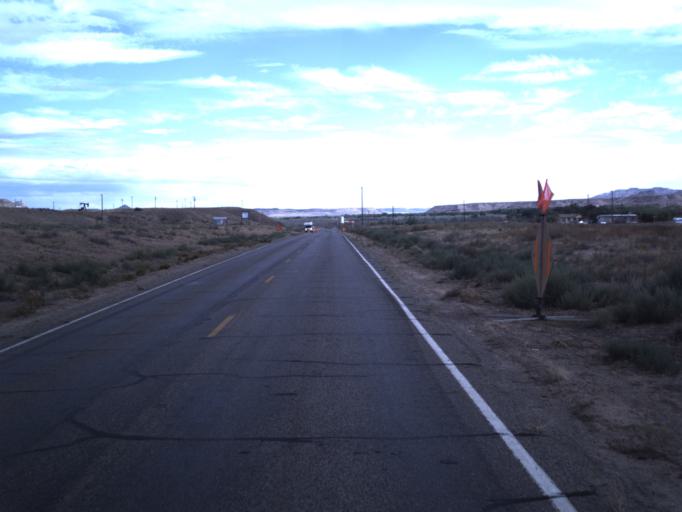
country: US
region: Utah
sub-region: San Juan County
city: Blanding
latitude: 37.2300
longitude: -109.2147
